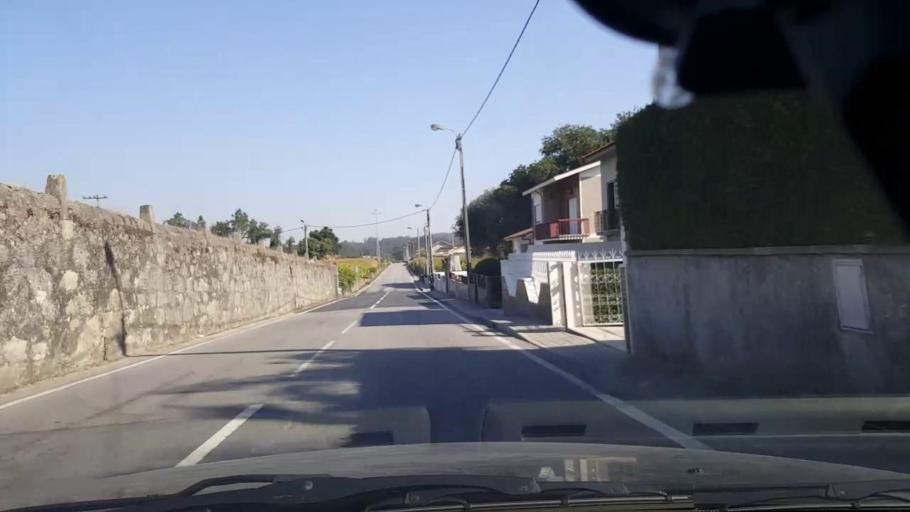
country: PT
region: Porto
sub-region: Vila do Conde
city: Arvore
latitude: 41.3424
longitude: -8.6807
